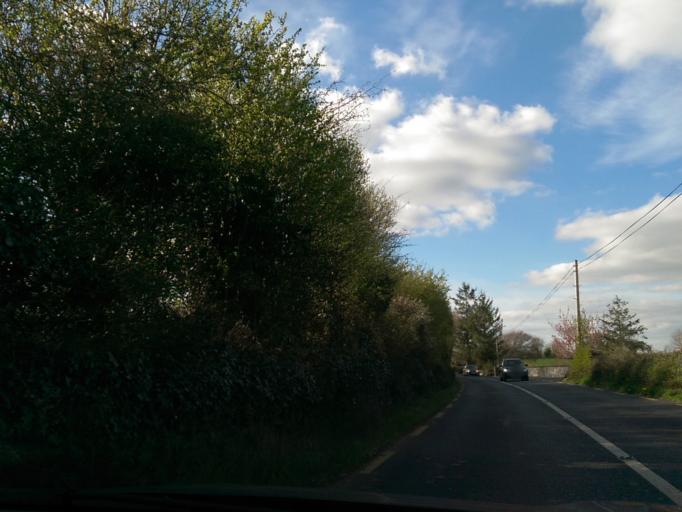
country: IE
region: Connaught
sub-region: County Galway
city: Portumna
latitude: 53.1206
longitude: -8.2409
